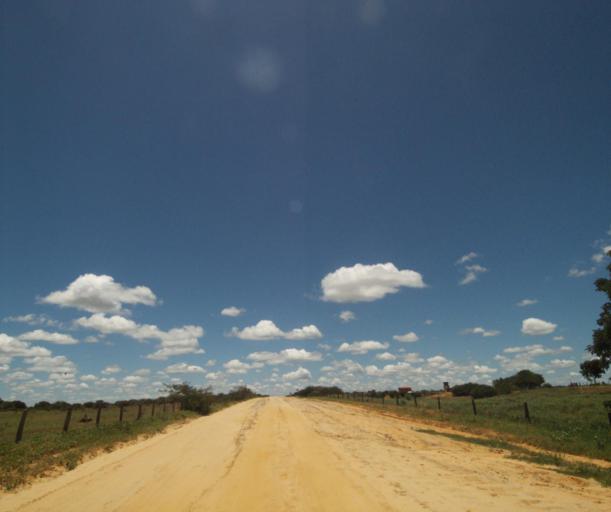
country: BR
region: Bahia
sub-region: Carinhanha
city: Carinhanha
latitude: -14.2808
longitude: -43.7932
